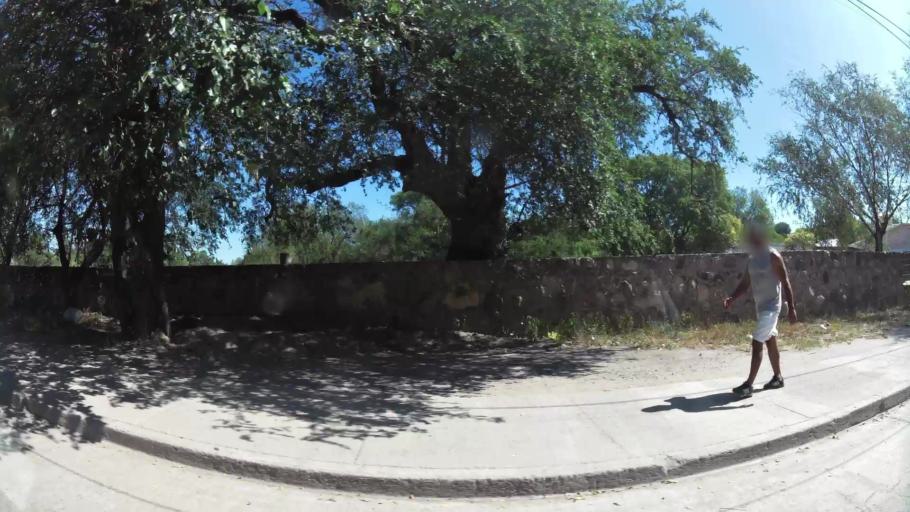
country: AR
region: Cordoba
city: Villa Allende
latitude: -31.2936
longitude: -64.3016
